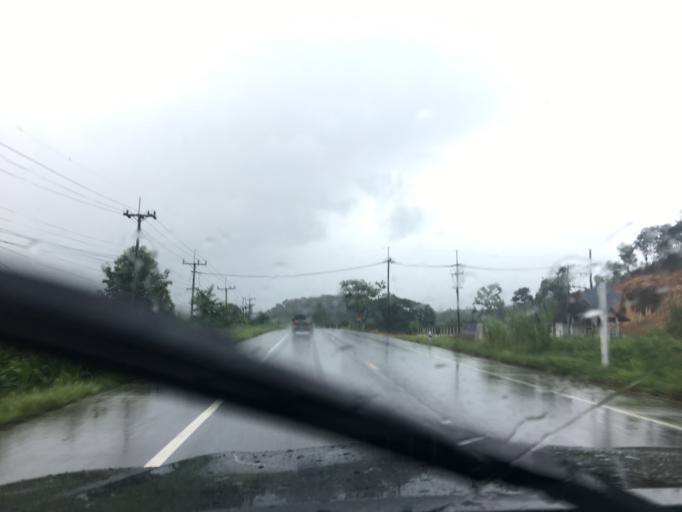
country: TH
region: Chiang Rai
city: Chiang Saen
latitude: 20.2790
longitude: 100.2103
